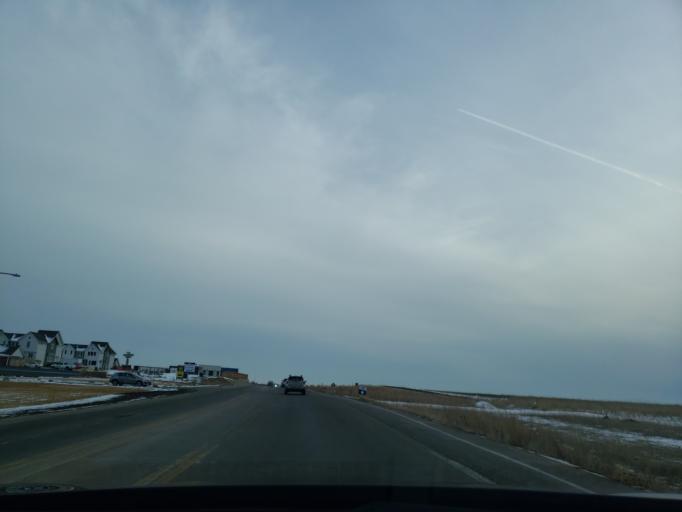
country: US
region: Colorado
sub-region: Larimer County
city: Campion
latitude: 40.3416
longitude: -105.0937
